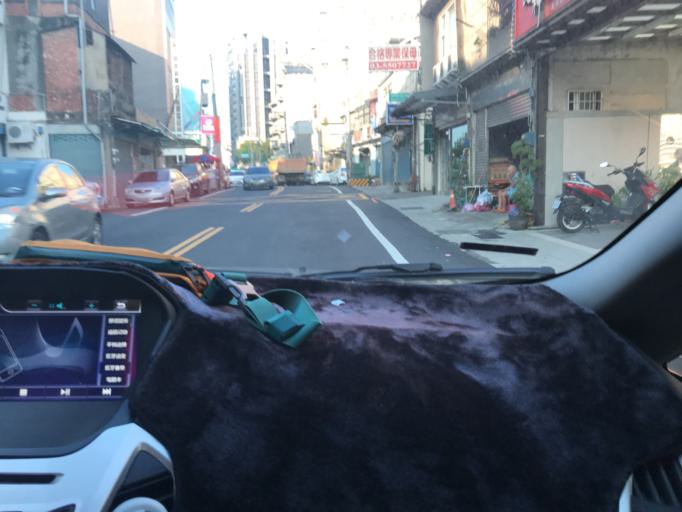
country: TW
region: Taiwan
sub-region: Hsinchu
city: Zhubei
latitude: 24.8216
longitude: 121.0321
